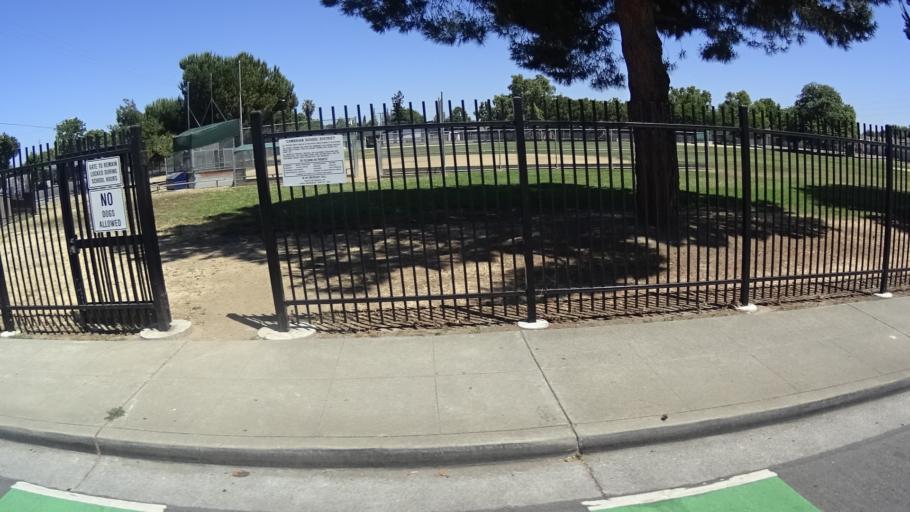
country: US
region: California
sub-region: Santa Clara County
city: Cambrian Park
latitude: 37.2761
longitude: -121.9221
